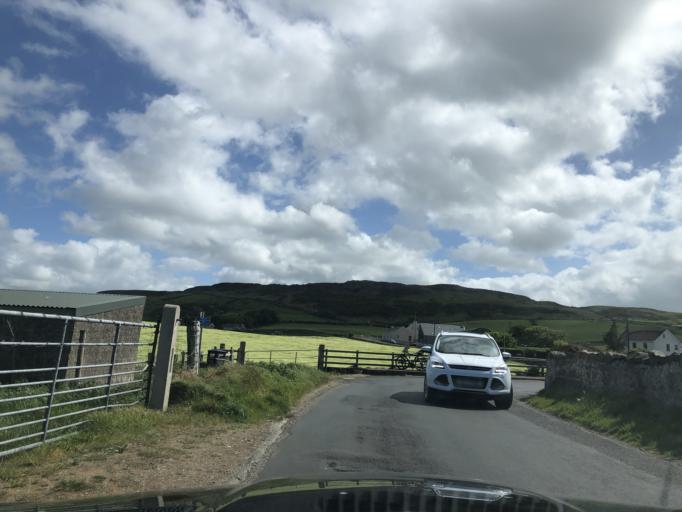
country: GB
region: Northern Ireland
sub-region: Moyle District
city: Ballycastle
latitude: 55.2403
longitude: -6.3661
